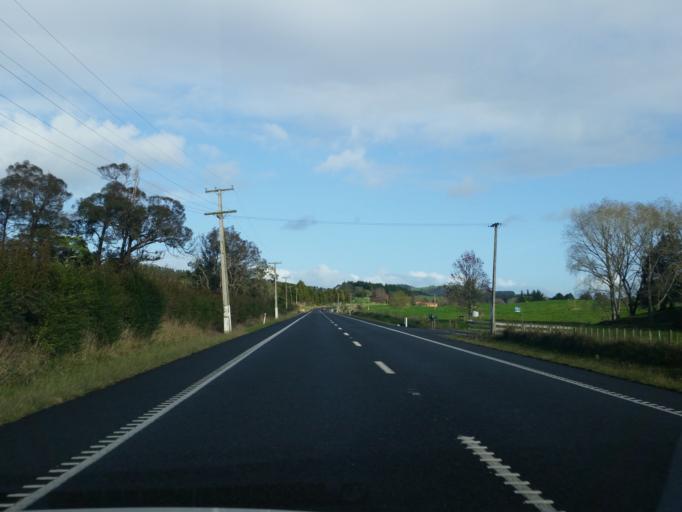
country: NZ
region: Waikato
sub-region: Hauraki District
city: Ngatea
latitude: -37.2878
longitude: 175.3886
